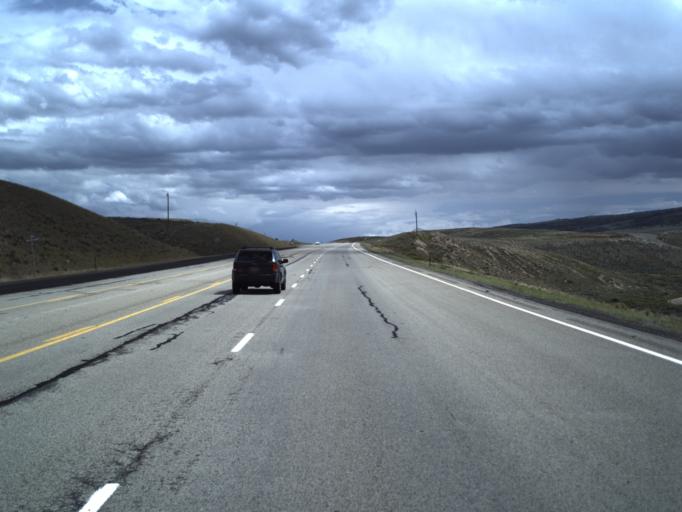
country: US
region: Utah
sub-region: Carbon County
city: Helper
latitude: 39.8522
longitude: -111.0128
